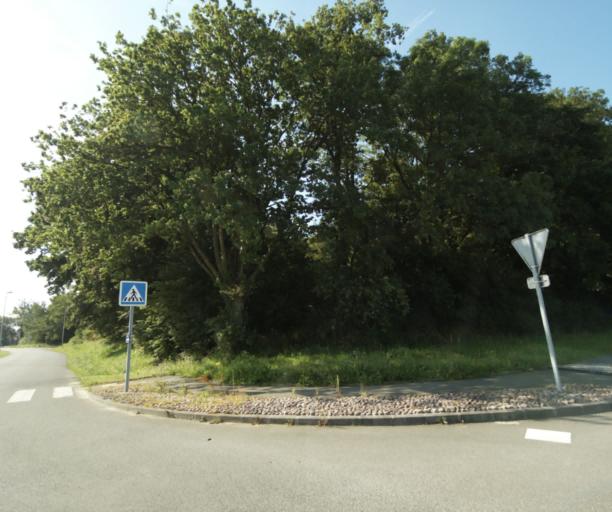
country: FR
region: Pays de la Loire
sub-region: Departement de la Mayenne
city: Laval
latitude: 48.0542
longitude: -0.7863
